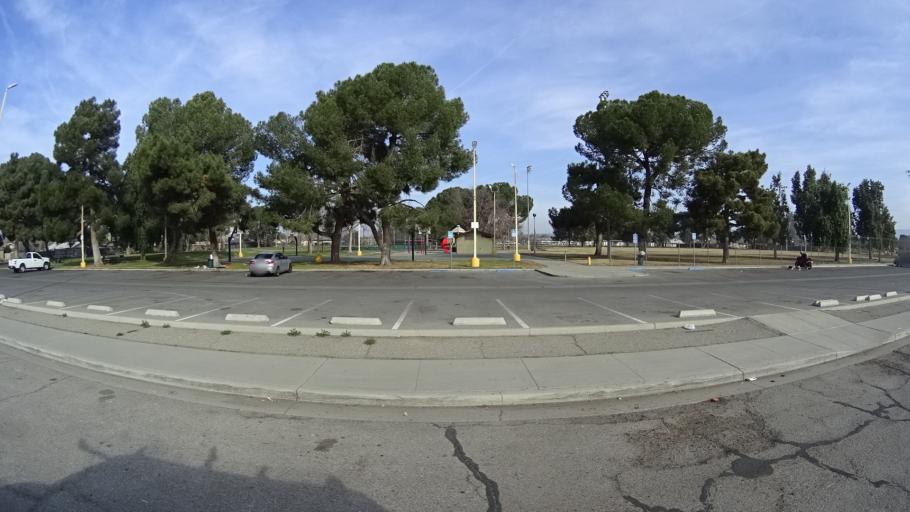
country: US
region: California
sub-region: Kern County
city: Bakersfield
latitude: 35.3614
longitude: -118.9709
